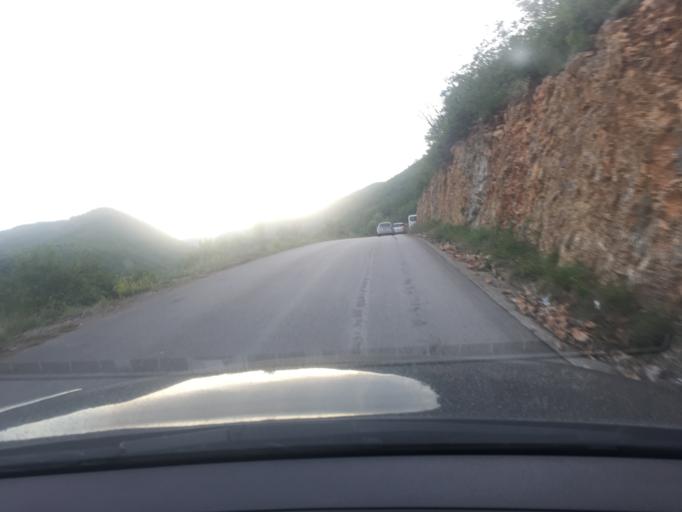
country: XK
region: Ferizaj
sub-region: Hani i Elezit
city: Hani i Elezit
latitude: 42.1446
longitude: 21.2873
